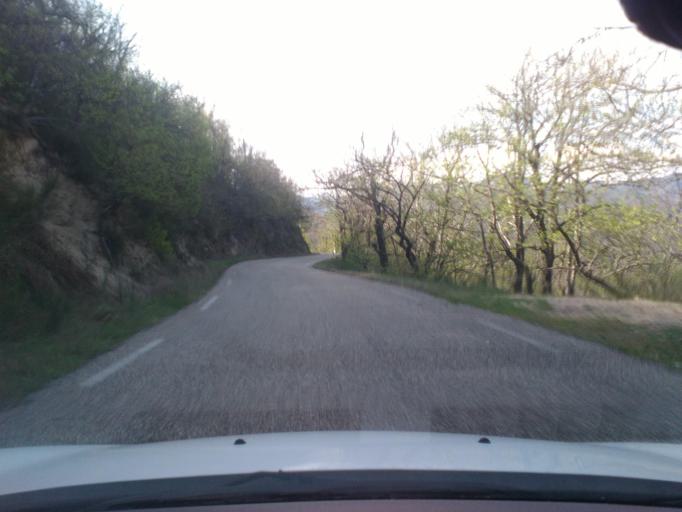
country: FR
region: Languedoc-Roussillon
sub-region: Departement du Gard
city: Lasalle
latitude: 44.0870
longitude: 3.8077
